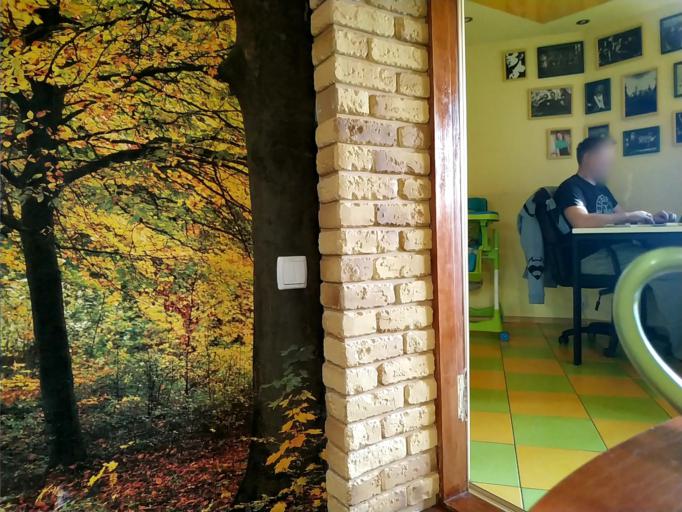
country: RU
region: Jaroslavl
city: Krasnyy Profintern
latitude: 57.8609
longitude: 40.6120
